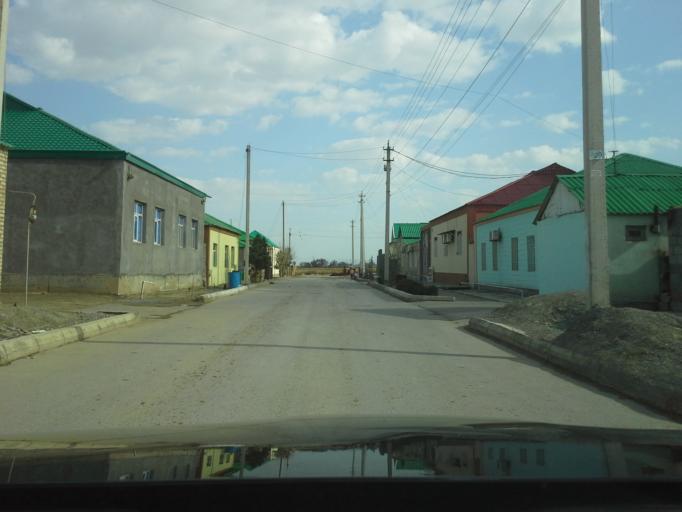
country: TM
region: Ahal
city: Ashgabat
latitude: 37.9886
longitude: 58.2934
